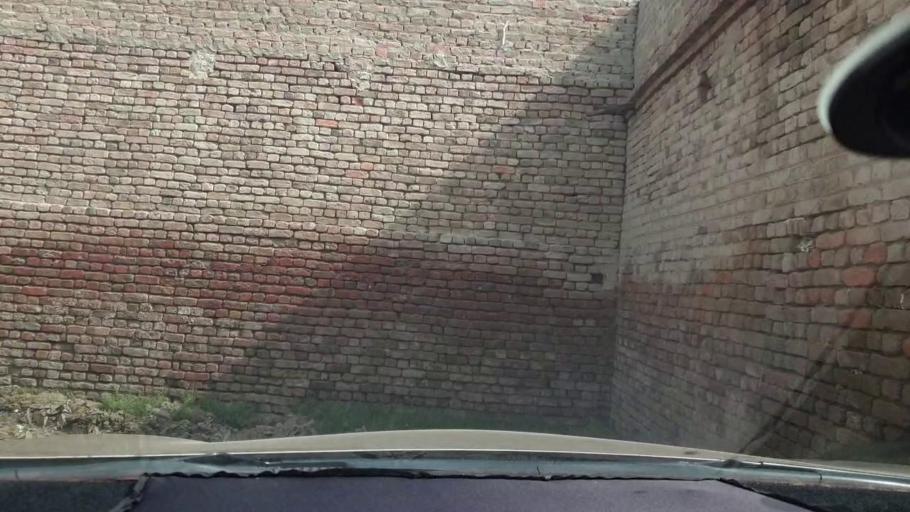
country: PK
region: Sindh
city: Kambar
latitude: 27.5426
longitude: 68.0468
